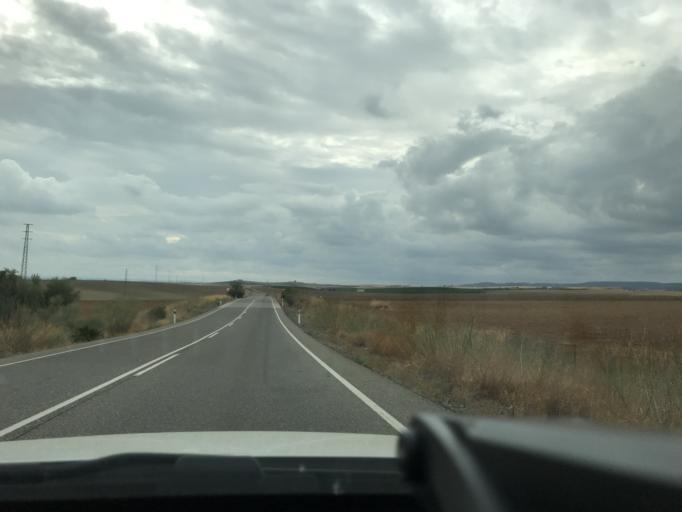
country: ES
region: Andalusia
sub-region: Provincia de Sevilla
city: Tocina
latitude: 37.6328
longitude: -5.7653
